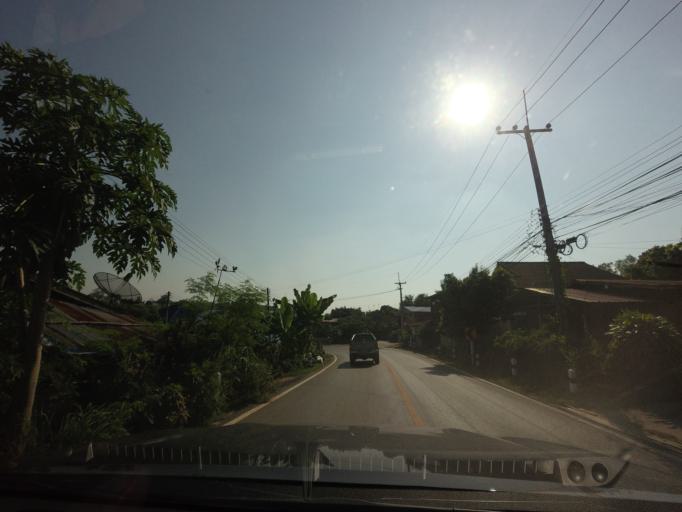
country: TH
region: Nan
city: Nan
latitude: 18.8071
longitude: 100.7997
